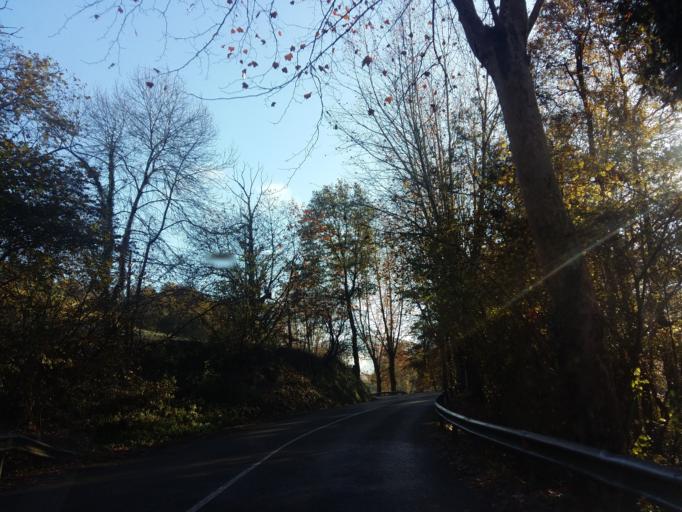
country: ES
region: Cantabria
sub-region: Provincia de Cantabria
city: Ramales de la Victoria
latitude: 43.2691
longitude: -3.4965
